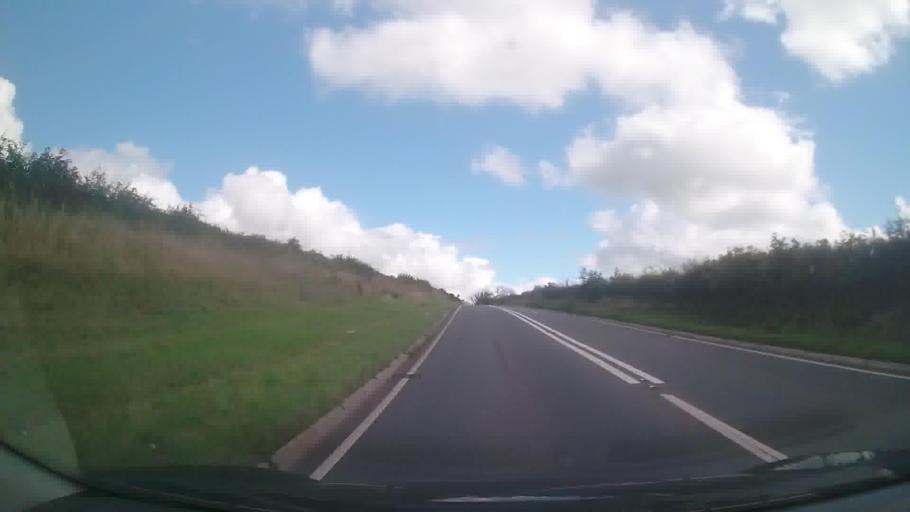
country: GB
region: Wales
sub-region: Pembrokeshire
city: Pembroke
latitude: 51.6820
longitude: -4.8874
